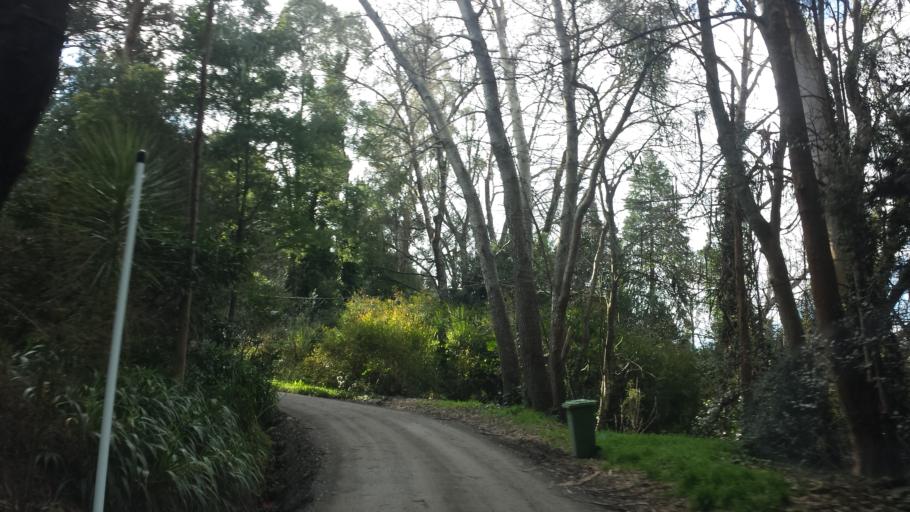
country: AU
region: Victoria
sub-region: Yarra Ranges
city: Kallista
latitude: -37.8844
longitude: 145.3797
